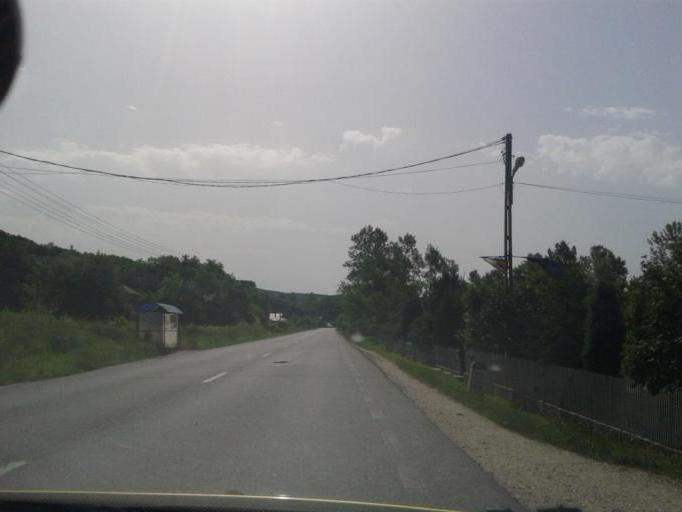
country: RO
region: Valcea
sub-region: Comuna Mihaesti
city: Mihaesti
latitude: 45.0683
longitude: 24.2261
